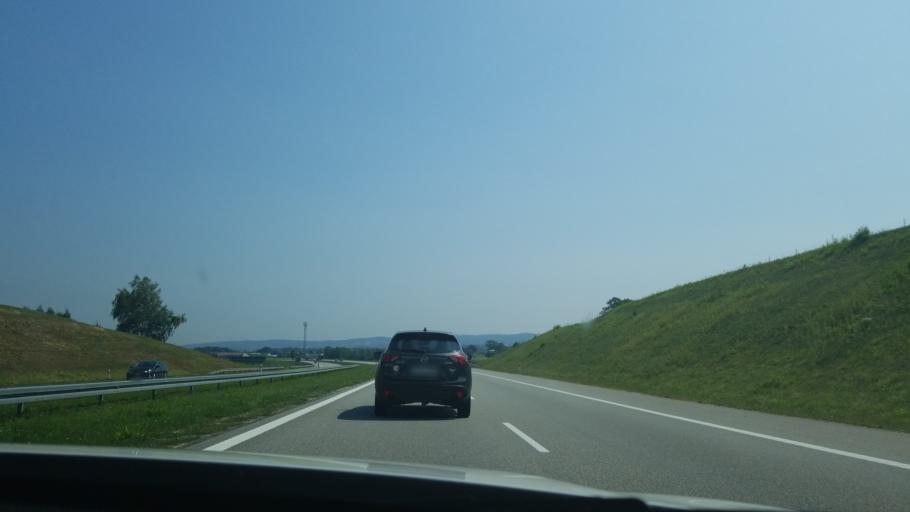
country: PL
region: Subcarpathian Voivodeship
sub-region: Powiat debicki
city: Zyrakow
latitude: 50.0814
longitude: 21.3622
